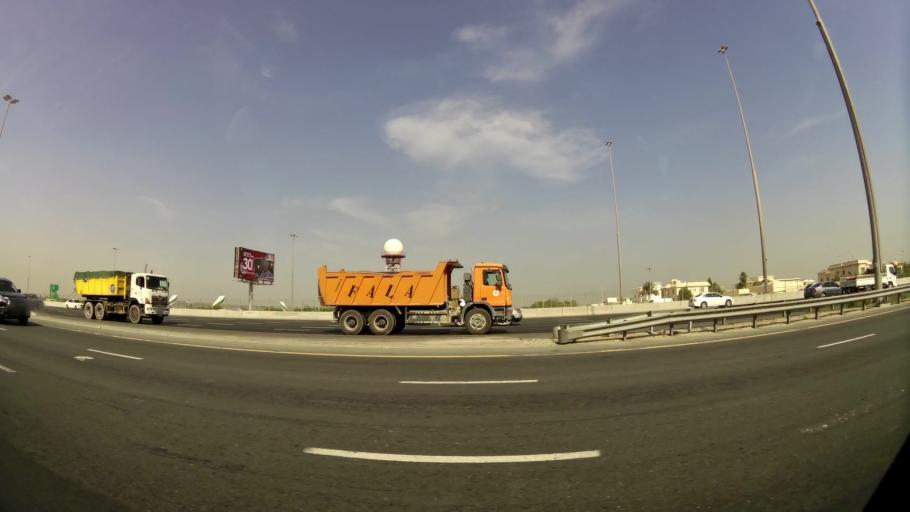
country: AE
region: Ash Shariqah
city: Sharjah
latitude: 25.2398
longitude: 55.4046
